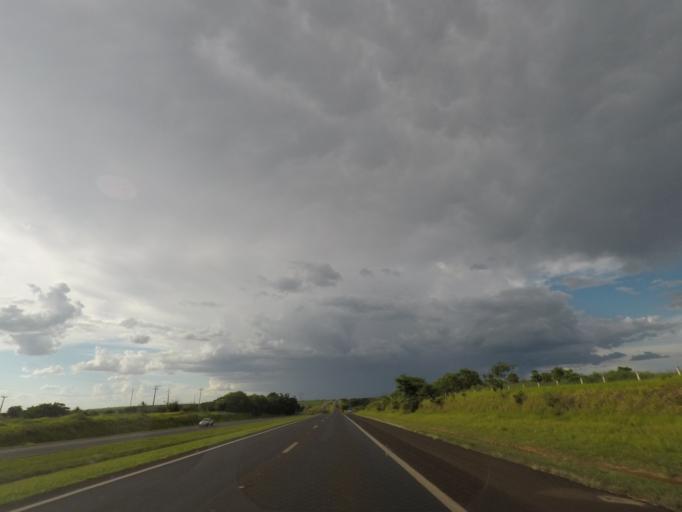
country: BR
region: Sao Paulo
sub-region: Jardinopolis
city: Jardinopolis
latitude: -21.0305
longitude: -47.8351
